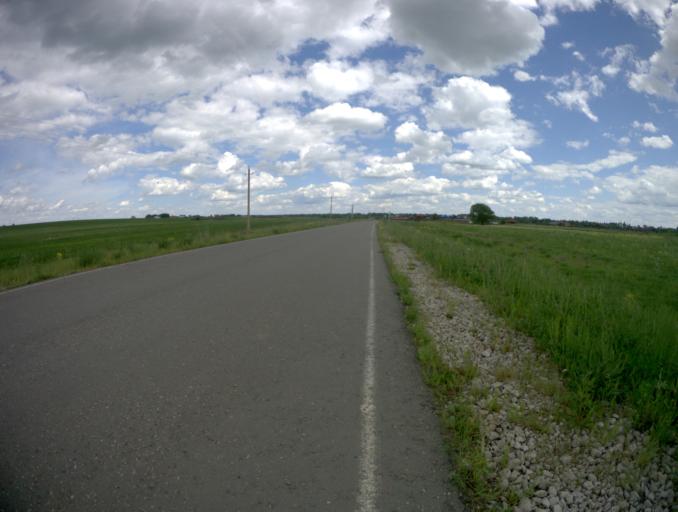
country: RU
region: Vladimir
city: Suzdal'
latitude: 56.4424
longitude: 40.4178
